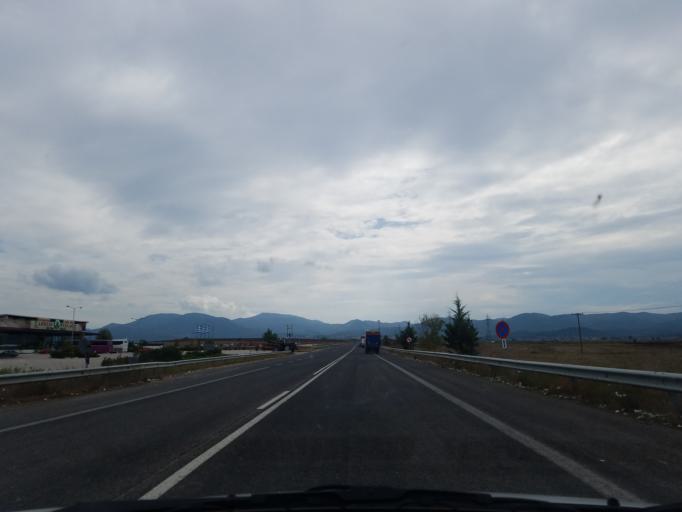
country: GR
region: Central Greece
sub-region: Nomos Fthiotidos
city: Omvriaki
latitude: 39.0686
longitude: 22.3237
